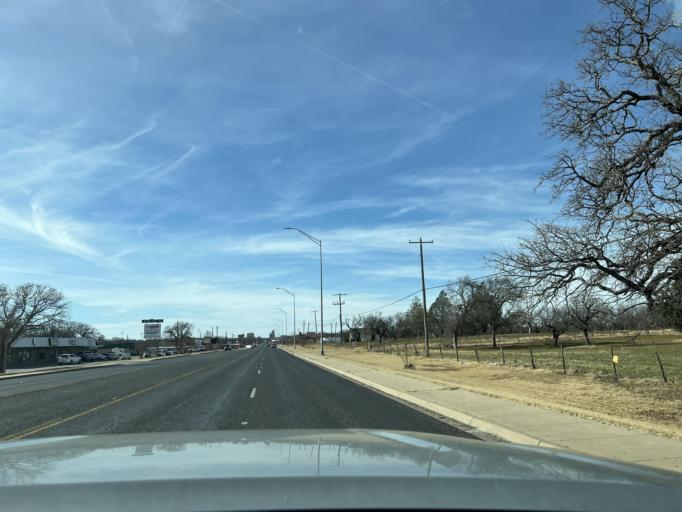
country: US
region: Texas
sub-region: Eastland County
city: Eastland
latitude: 32.4019
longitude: -98.8021
